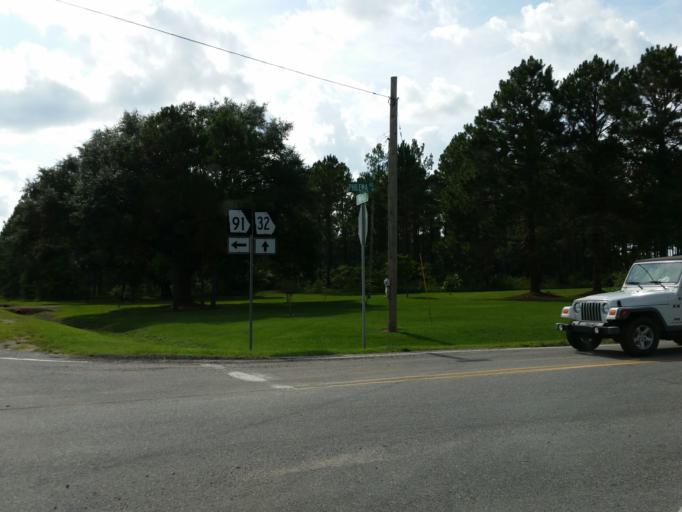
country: US
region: Georgia
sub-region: Lee County
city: Leesburg
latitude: 31.7267
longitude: -84.0470
